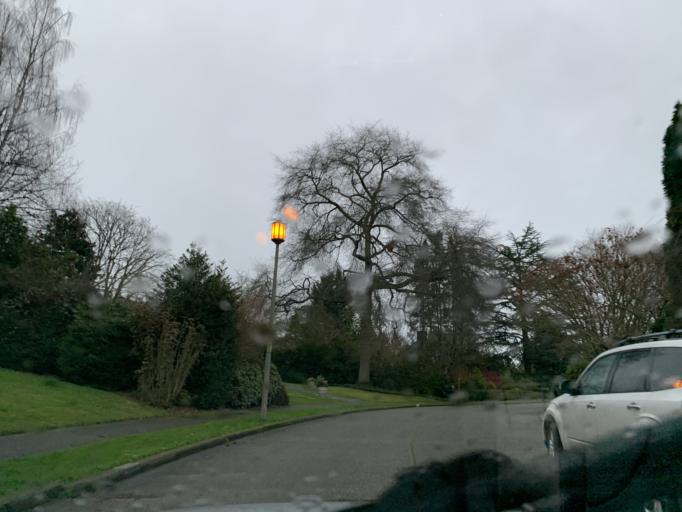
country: US
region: Washington
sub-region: King County
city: Yarrow Point
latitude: 47.6677
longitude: -122.2654
